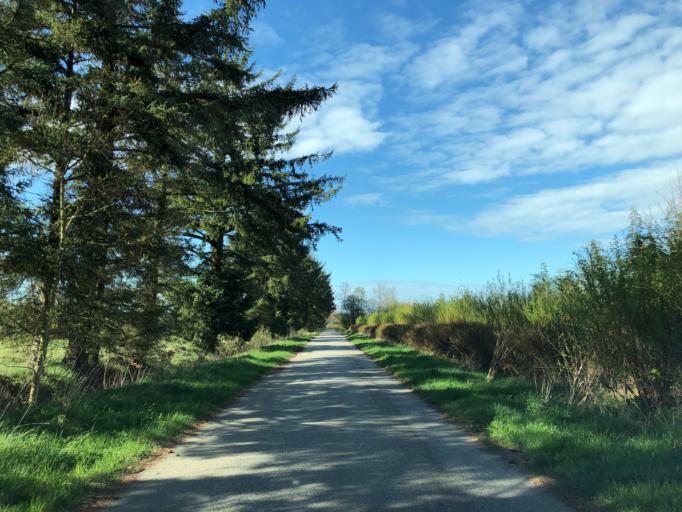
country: DK
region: Central Jutland
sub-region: Holstebro Kommune
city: Ulfborg
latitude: 56.2565
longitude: 8.3278
